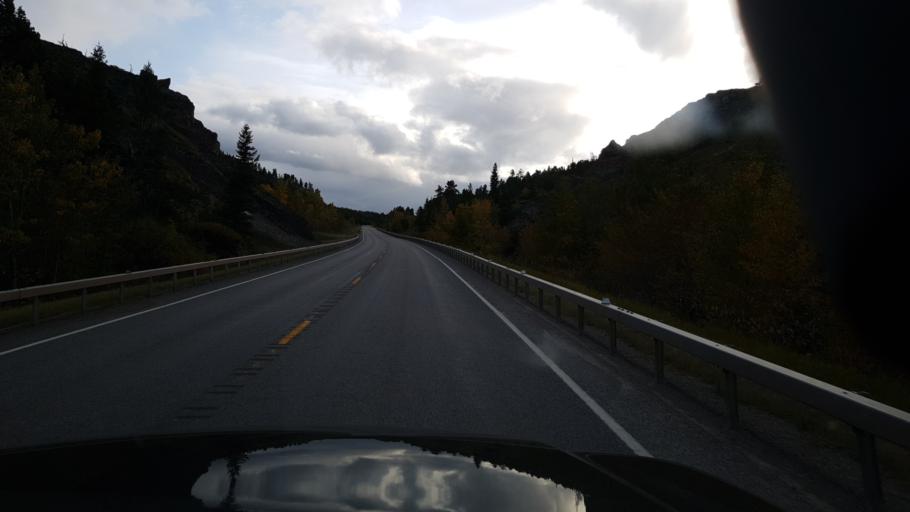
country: US
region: Montana
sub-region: Glacier County
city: South Browning
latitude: 48.3995
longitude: -113.2524
